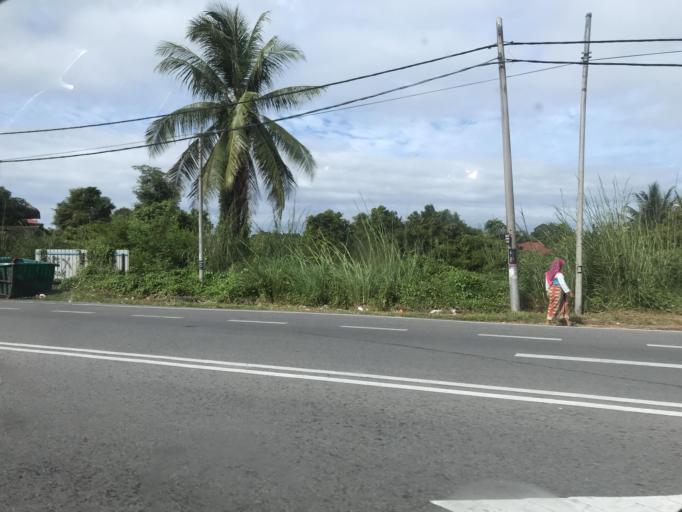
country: MY
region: Kelantan
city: Kota Bharu
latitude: 6.1255
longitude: 102.1818
